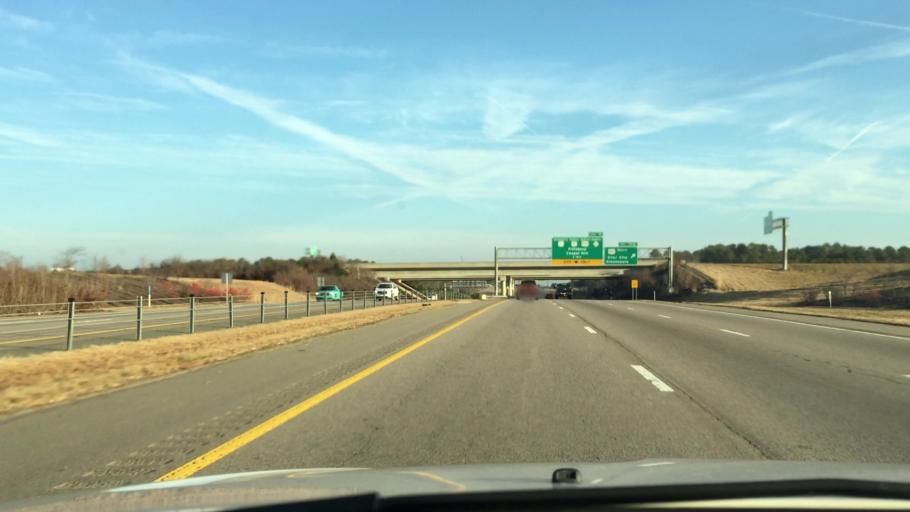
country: US
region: North Carolina
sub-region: Lee County
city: Sanford
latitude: 35.5090
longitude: -79.1886
